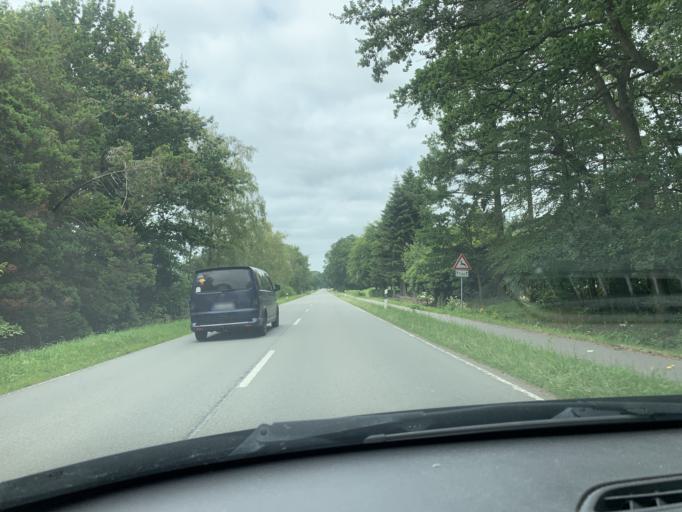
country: DE
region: Lower Saxony
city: Bad Zwischenahn
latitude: 53.2406
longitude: 7.9850
